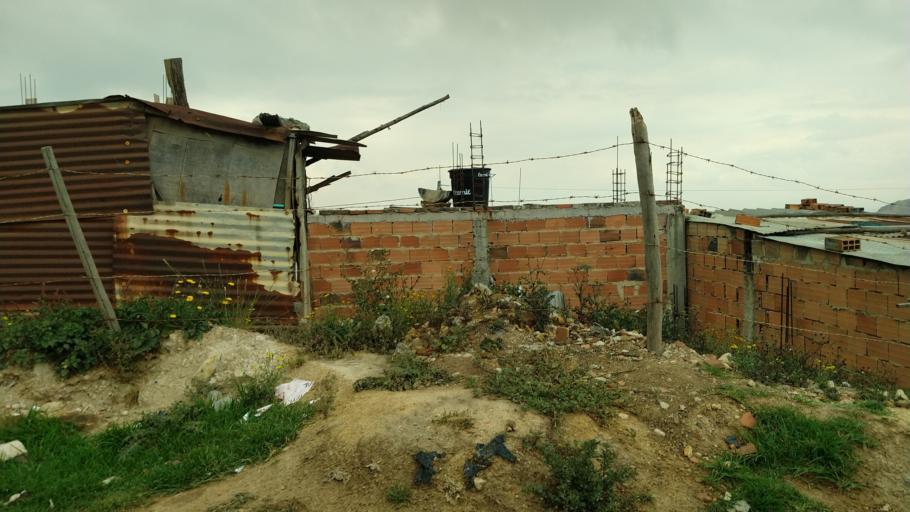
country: CO
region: Cundinamarca
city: Soacha
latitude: 4.5554
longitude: -74.2123
